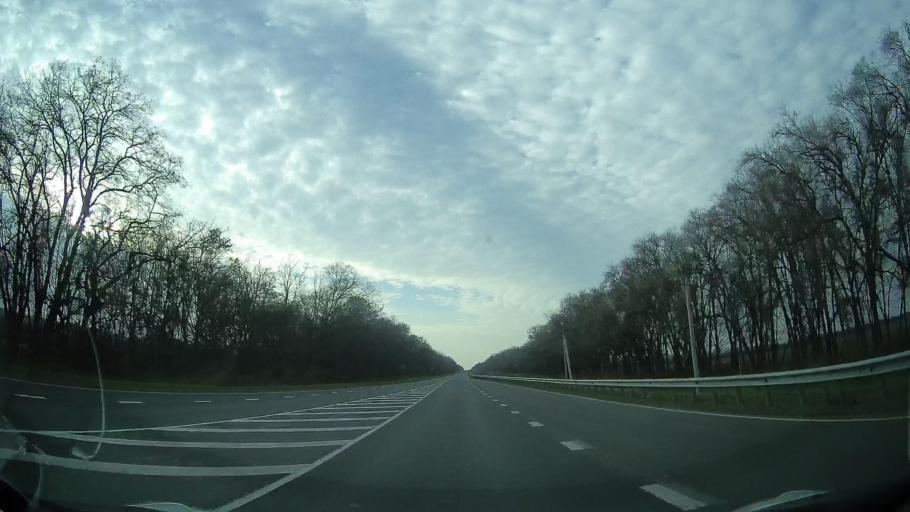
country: RU
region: Rostov
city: Bagayevskaya
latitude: 47.0928
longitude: 40.3903
